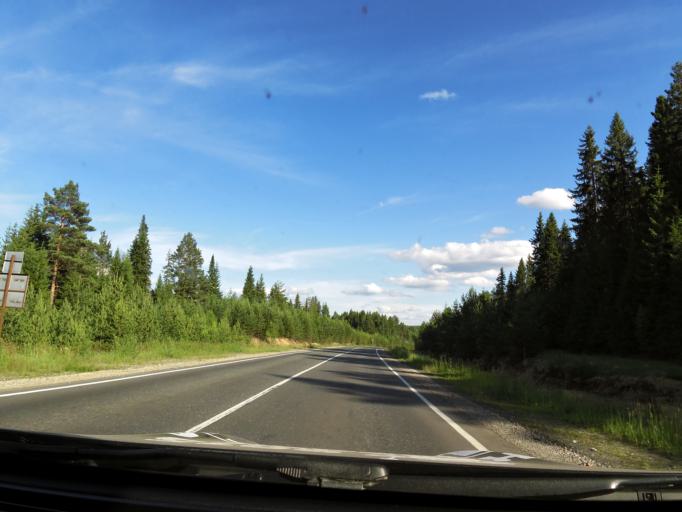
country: RU
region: Kirov
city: Chernaya Kholunitsa
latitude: 58.8513
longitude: 51.7394
